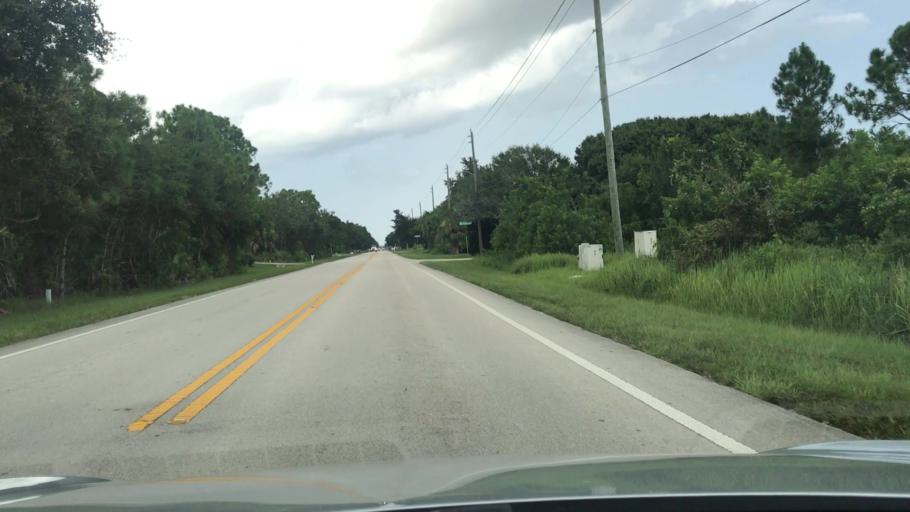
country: US
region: Florida
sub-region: Indian River County
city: Sebastian
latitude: 27.7821
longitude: -80.4974
